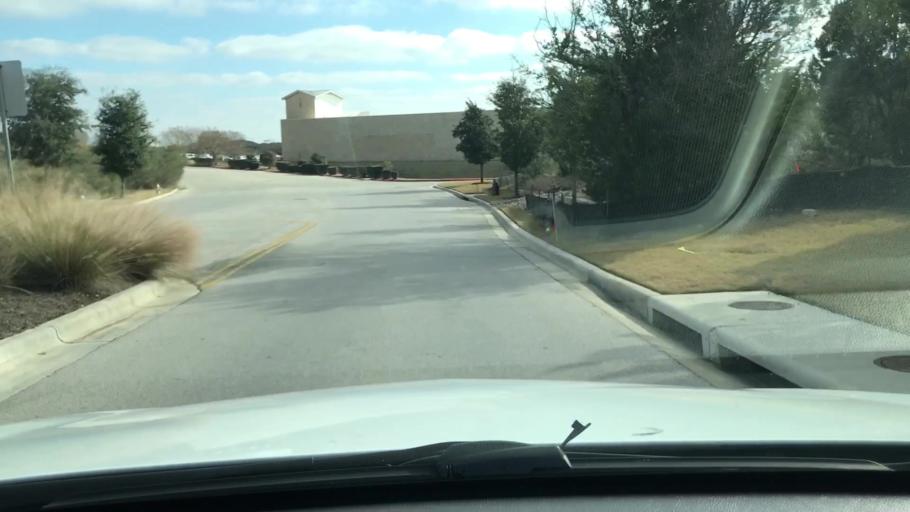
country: US
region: Texas
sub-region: Travis County
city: Bee Cave
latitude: 30.3169
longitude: -97.9564
